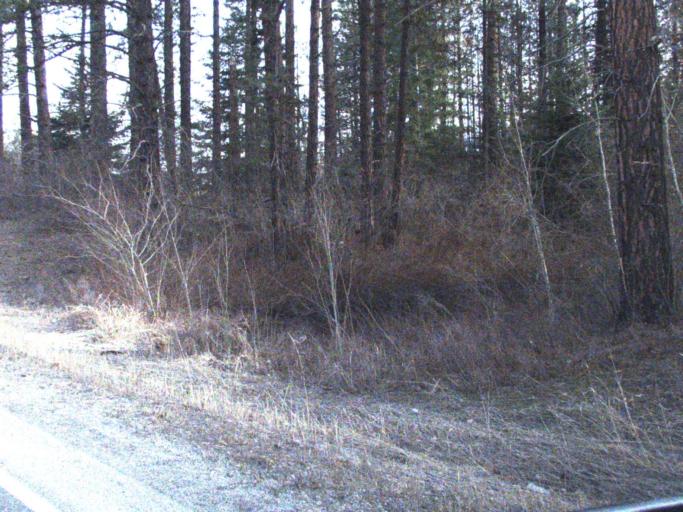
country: US
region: Washington
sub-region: Pend Oreille County
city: Newport
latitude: 48.3092
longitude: -117.2866
